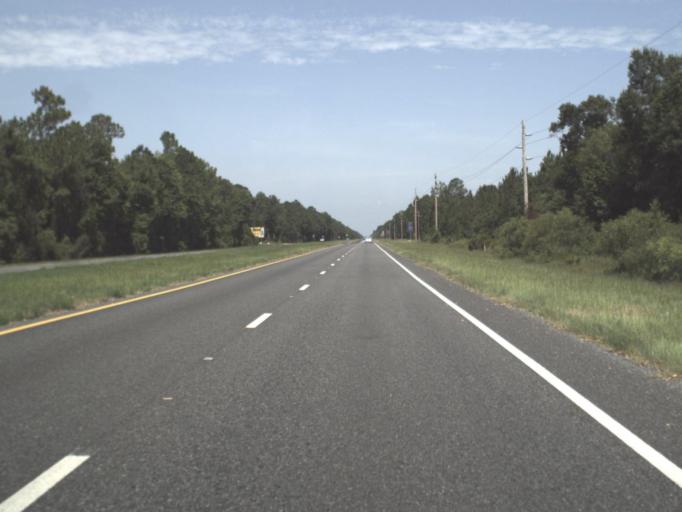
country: US
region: Florida
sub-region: Dixie County
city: Cross City
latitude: 29.6527
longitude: -83.1720
